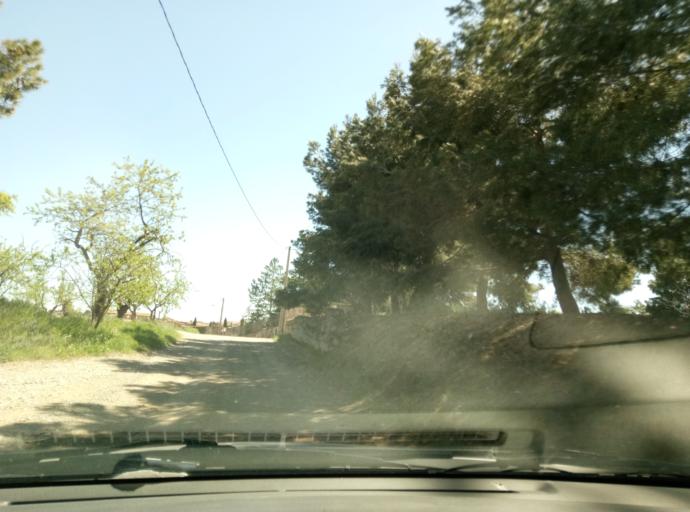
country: ES
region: Catalonia
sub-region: Provincia de Lleida
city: Vinaixa
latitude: 41.4209
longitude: 0.9328
